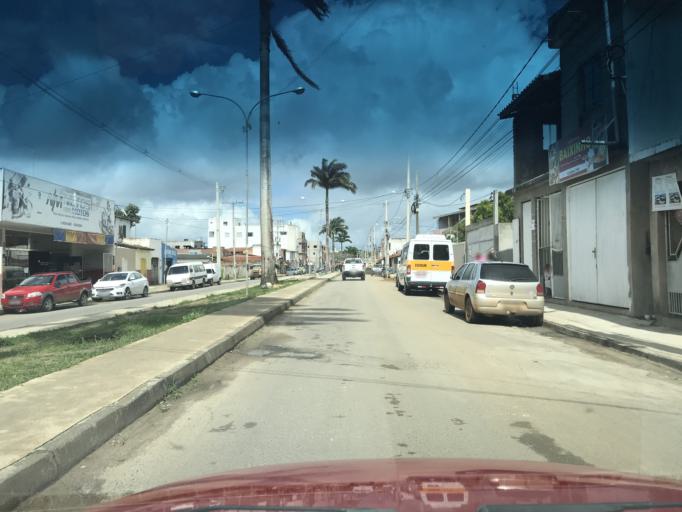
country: BR
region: Bahia
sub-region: Santo Antonio De Jesus
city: Santo Antonio de Jesus
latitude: -12.9763
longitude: -39.2747
